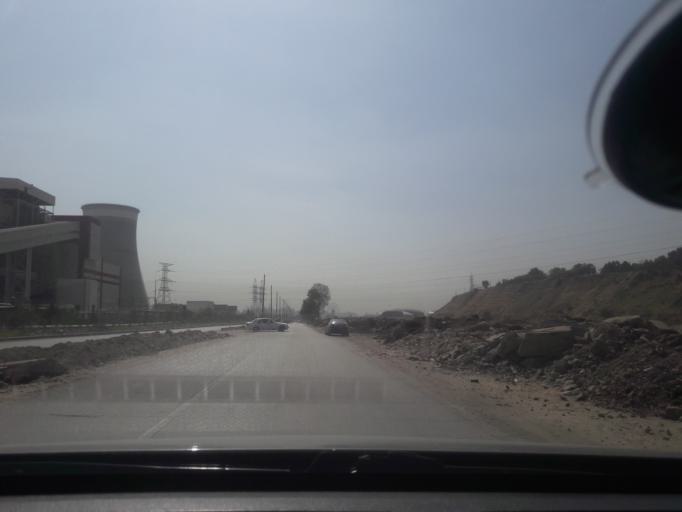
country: TJ
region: Dushanbe
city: Dushanbe
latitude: 38.6117
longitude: 68.7701
